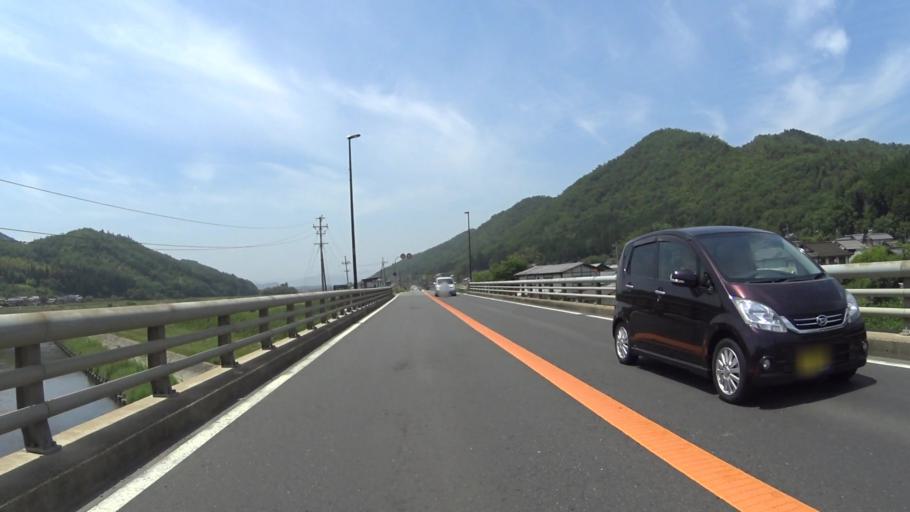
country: JP
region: Kyoto
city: Ayabe
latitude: 35.2513
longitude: 135.2092
